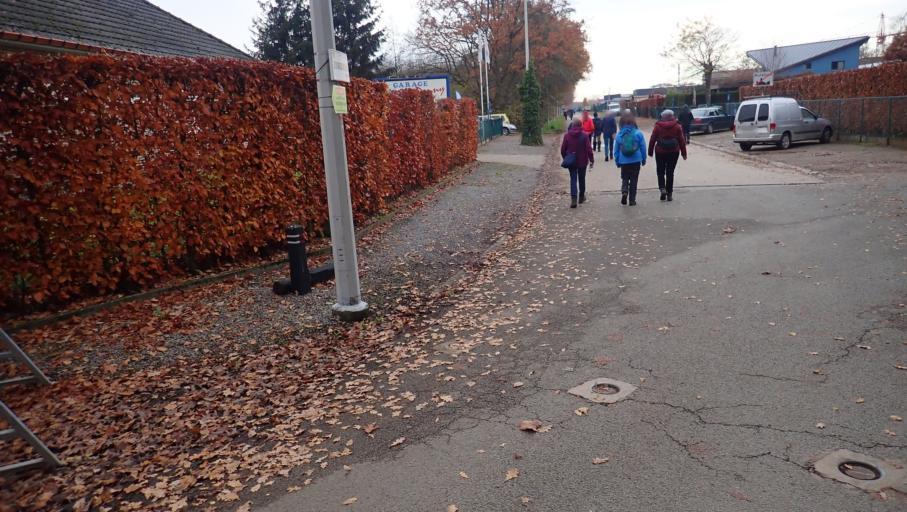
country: BE
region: Flanders
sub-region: Provincie Antwerpen
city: Hulshout
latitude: 51.0763
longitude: 4.8154
